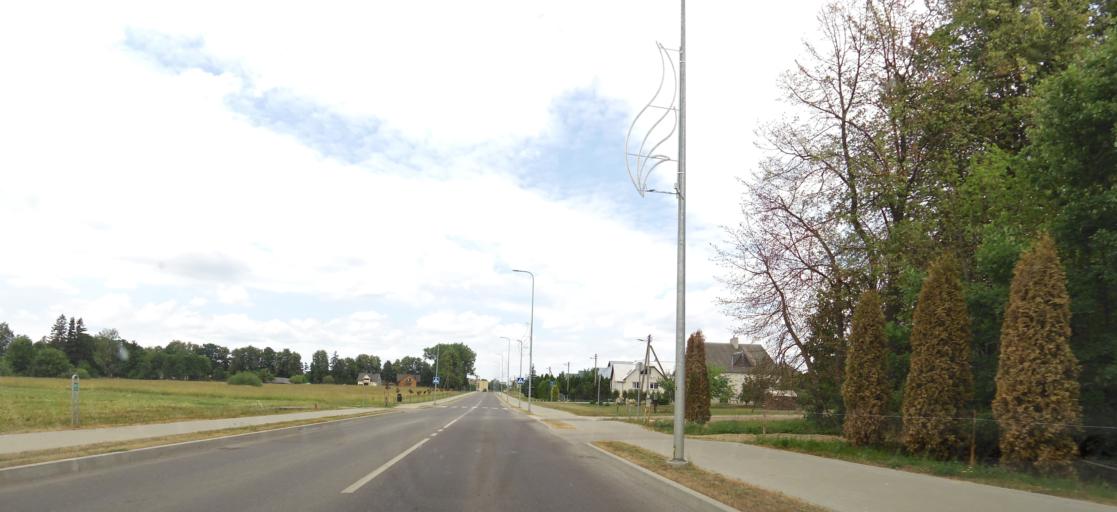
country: LT
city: Sirvintos
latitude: 55.0427
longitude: 24.9666
